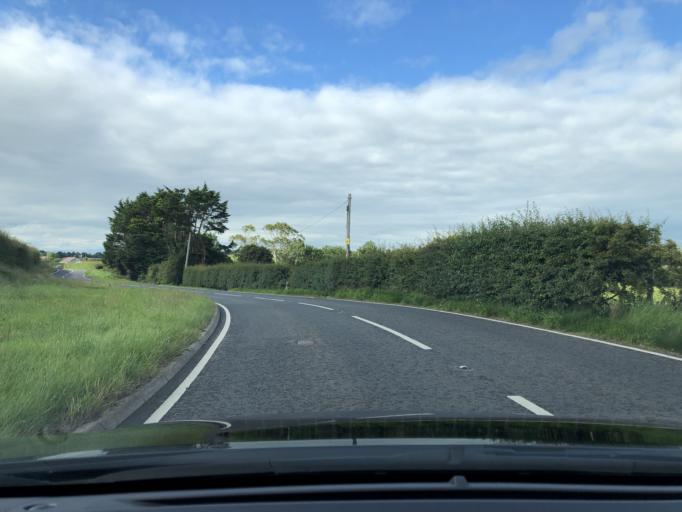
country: GB
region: Northern Ireland
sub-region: Down District
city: Dundrum
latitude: 54.2656
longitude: -5.7829
